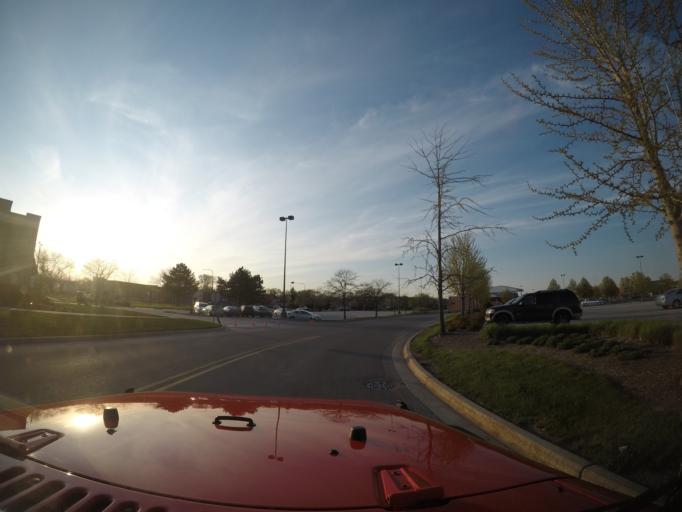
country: US
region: Illinois
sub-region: Cook County
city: Prospect Heights
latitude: 42.0819
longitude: -87.9359
